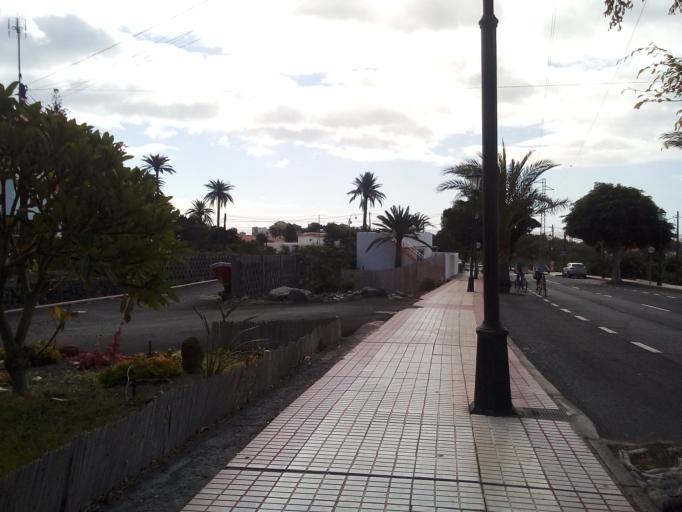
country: ES
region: Canary Islands
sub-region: Provincia de Santa Cruz de Tenerife
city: Alajero
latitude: 28.0911
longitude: -17.3357
